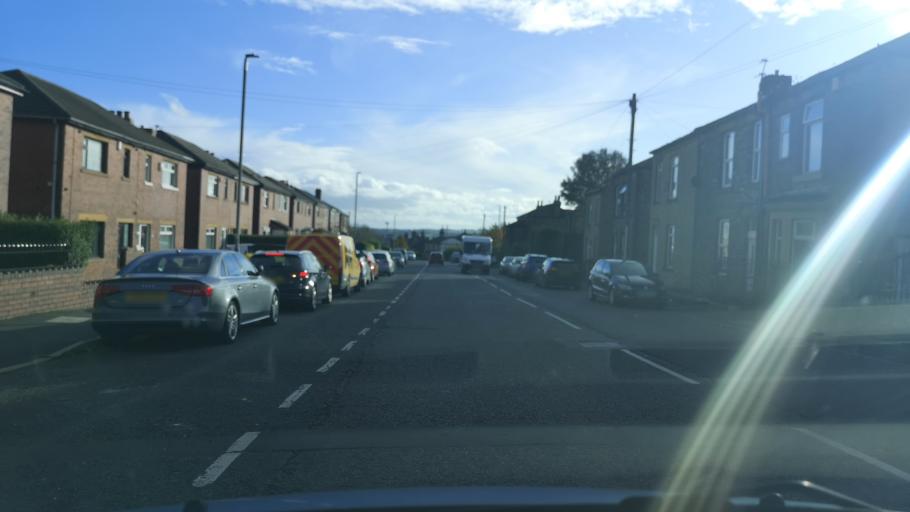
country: GB
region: England
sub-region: Kirklees
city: Batley
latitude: 53.7025
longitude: -1.6550
